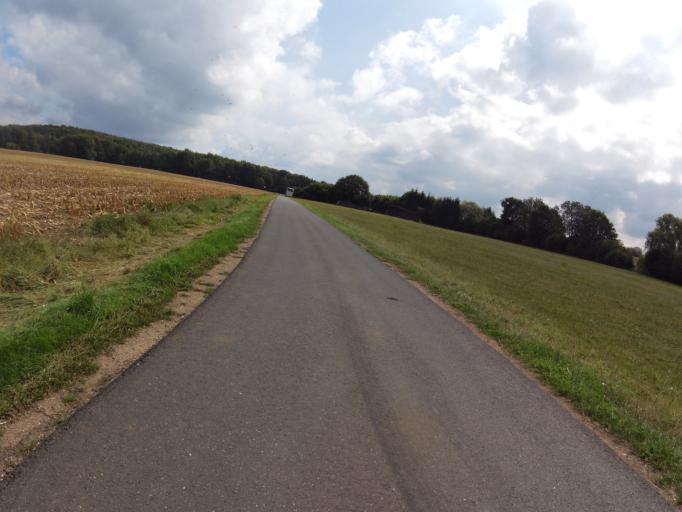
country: DE
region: Rheinland-Pfalz
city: Oberbettingen
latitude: 50.2771
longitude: 6.6502
